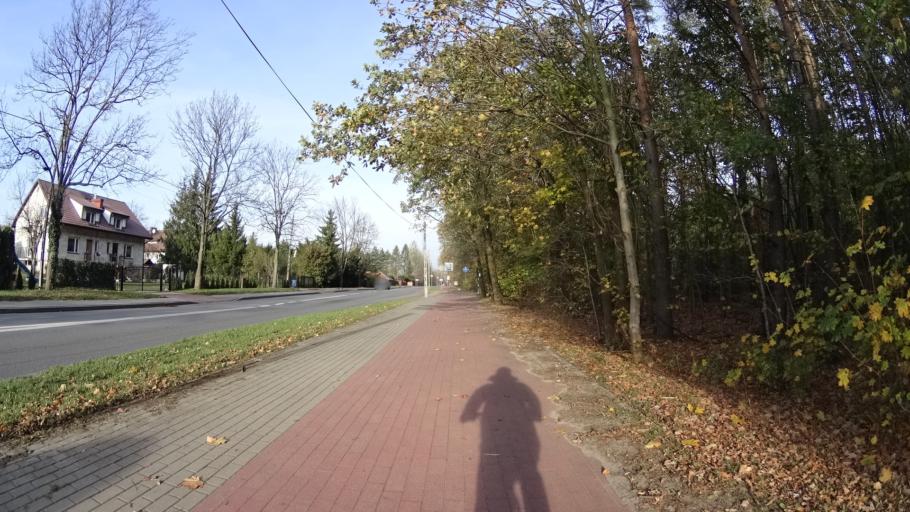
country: PL
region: Masovian Voivodeship
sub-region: Powiat warszawski zachodni
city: Babice
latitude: 52.2649
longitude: 20.8573
